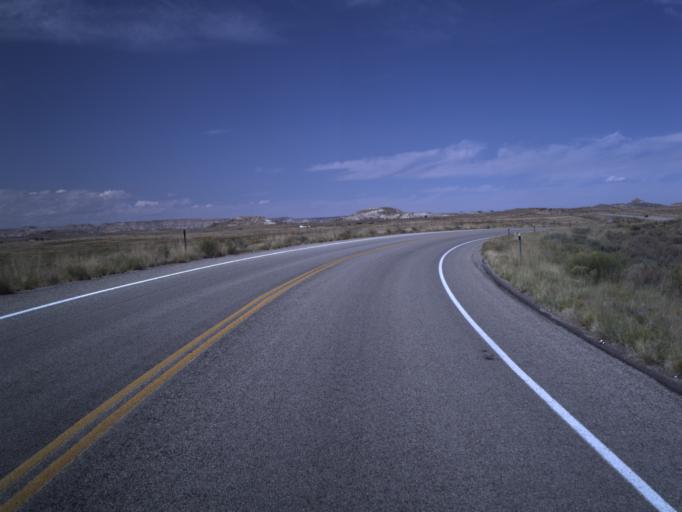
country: US
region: Colorado
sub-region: Montezuma County
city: Towaoc
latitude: 37.1556
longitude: -109.0550
